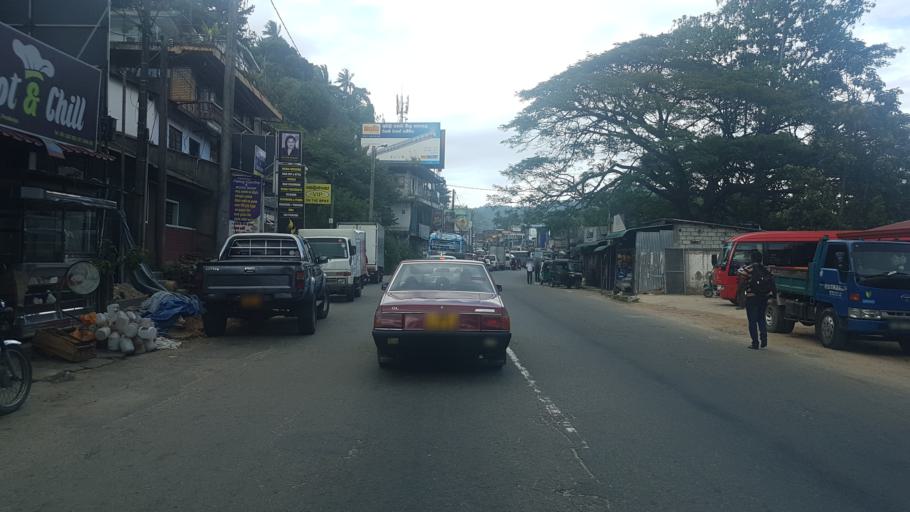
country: LK
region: Central
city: Kandy
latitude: 7.2620
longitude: 80.5930
